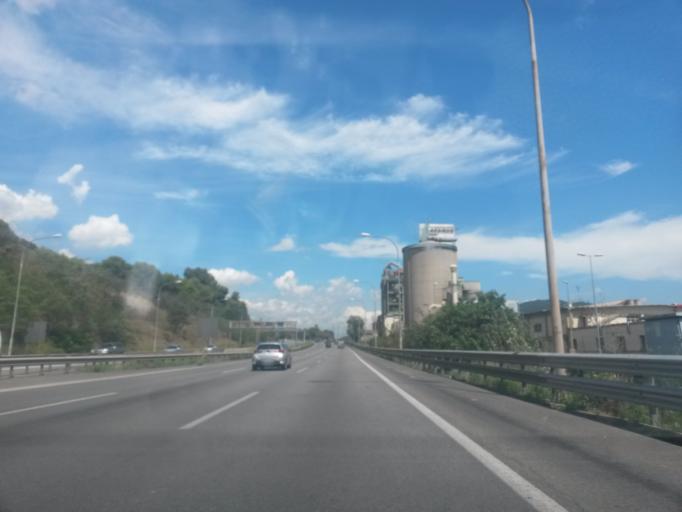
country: ES
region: Catalonia
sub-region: Provincia de Barcelona
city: Montcada i Reixac
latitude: 41.4719
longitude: 2.1797
